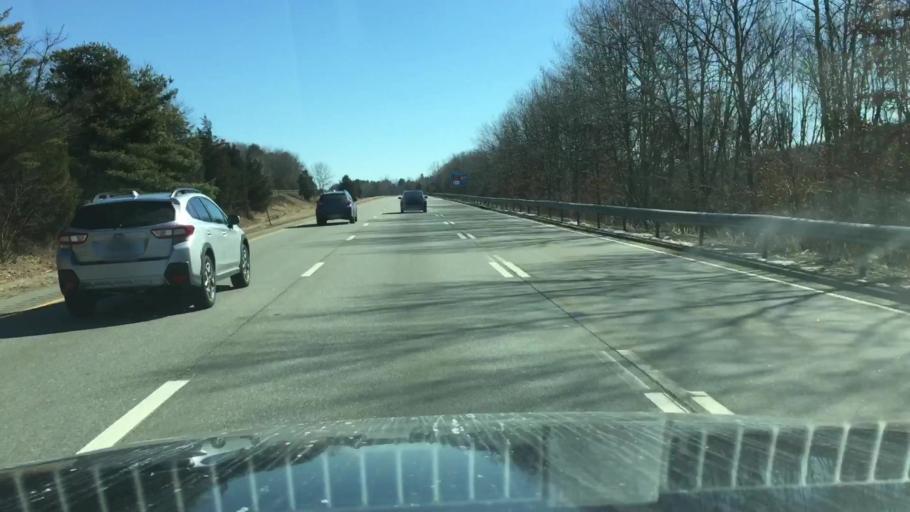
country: US
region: Connecticut
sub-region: New London County
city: Colchester
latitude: 41.5773
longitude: -72.3518
